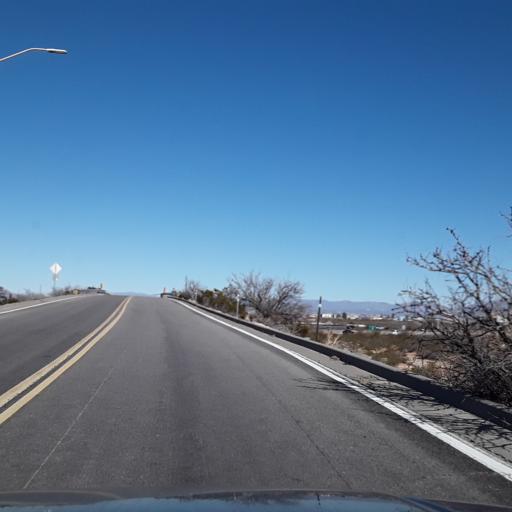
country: US
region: New Mexico
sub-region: Dona Ana County
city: Mesilla
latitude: 32.2807
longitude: -106.8840
